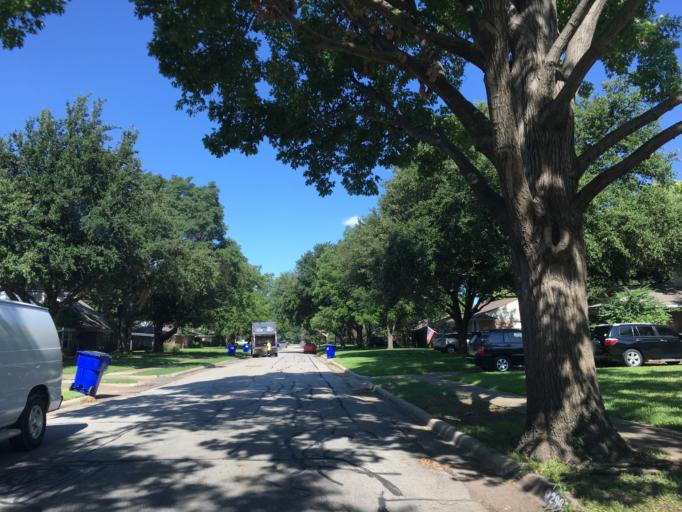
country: US
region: Texas
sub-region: Dallas County
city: Farmers Branch
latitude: 32.9192
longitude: -96.8780
